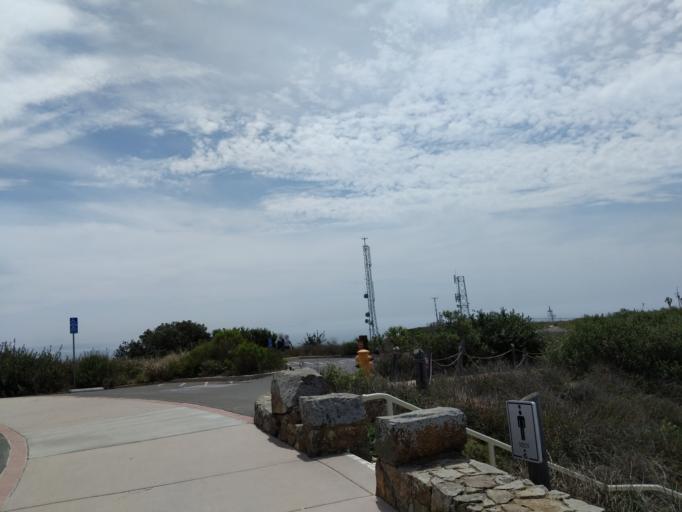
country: US
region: California
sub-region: San Diego County
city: Coronado
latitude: 32.6717
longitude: -117.2411
